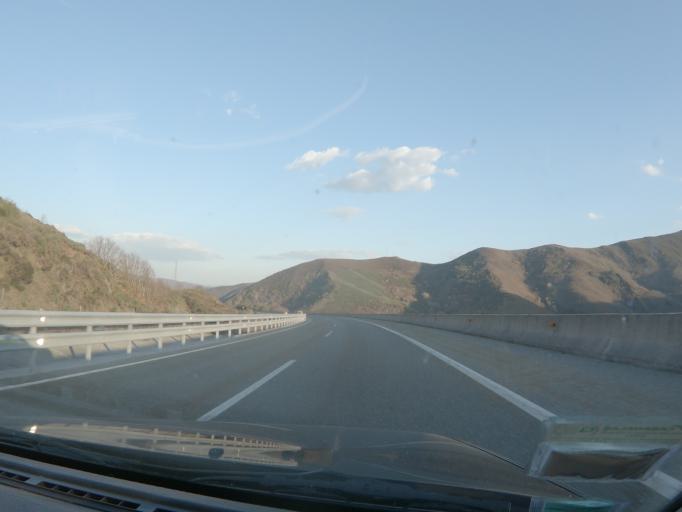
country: ES
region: Castille and Leon
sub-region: Provincia de Leon
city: Vega de Valcarce
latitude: 42.6755
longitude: -6.9863
